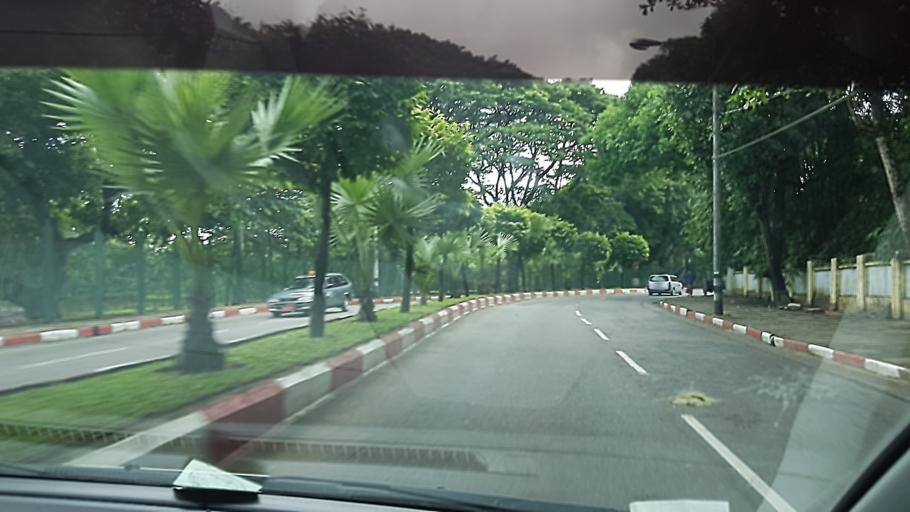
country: MM
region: Yangon
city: Yangon
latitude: 16.7950
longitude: 96.1584
